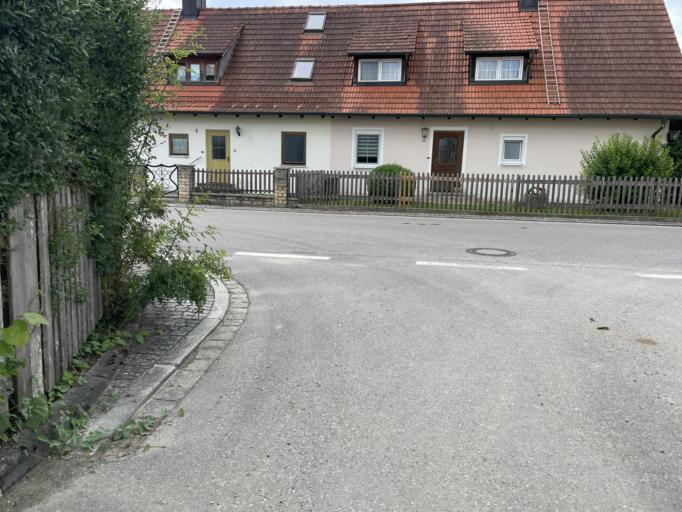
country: DE
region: Bavaria
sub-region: Upper Bavaria
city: Peissenberg
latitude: 47.7866
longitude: 11.0663
